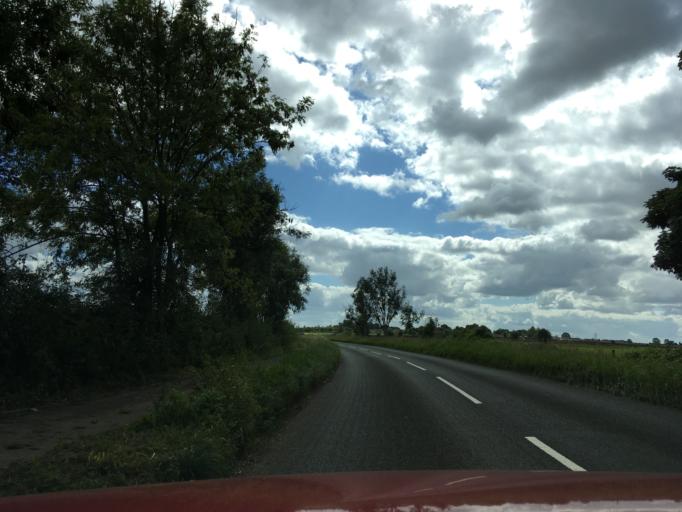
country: GB
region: England
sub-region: Wiltshire
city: Colerne
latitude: 51.4495
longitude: -2.2582
